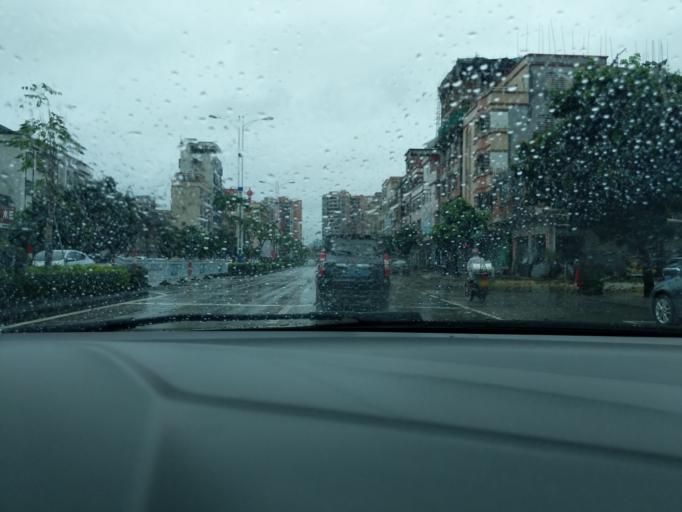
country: CN
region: Guangdong
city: Pingshi
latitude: 22.1998
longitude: 112.3309
